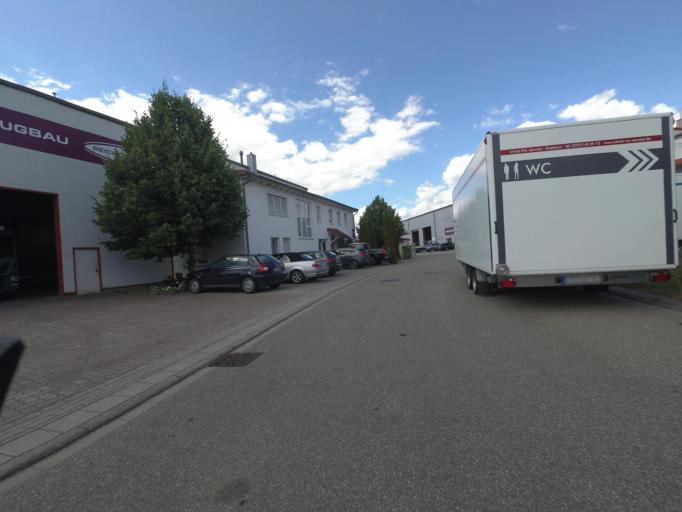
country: DE
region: Baden-Wuerttemberg
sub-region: Karlsruhe Region
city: Sinzheim
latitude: 48.7780
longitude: 8.1729
